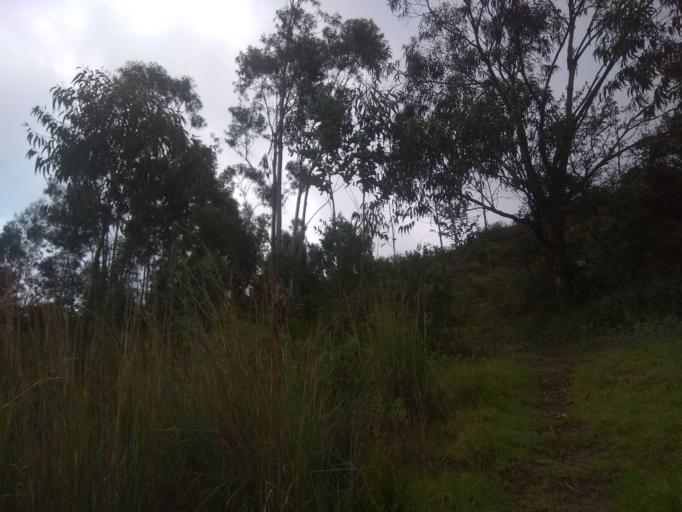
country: CO
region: Boyaca
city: Socha Viejo
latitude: 6.0091
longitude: -72.6756
